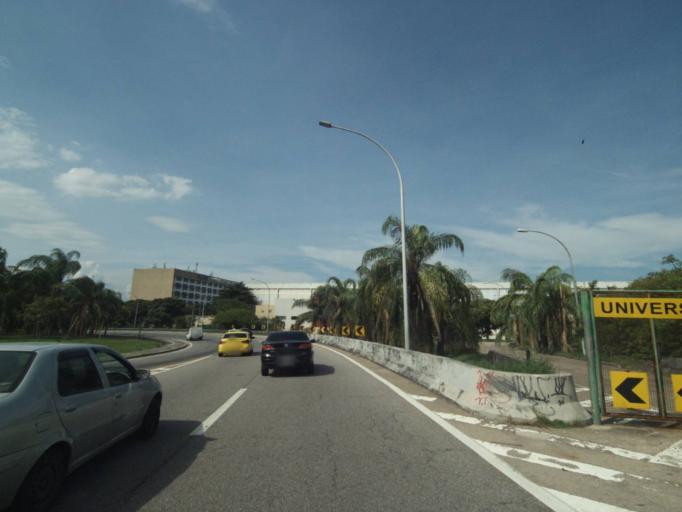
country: BR
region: Rio de Janeiro
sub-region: Rio De Janeiro
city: Rio de Janeiro
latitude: -22.8618
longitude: -43.2323
